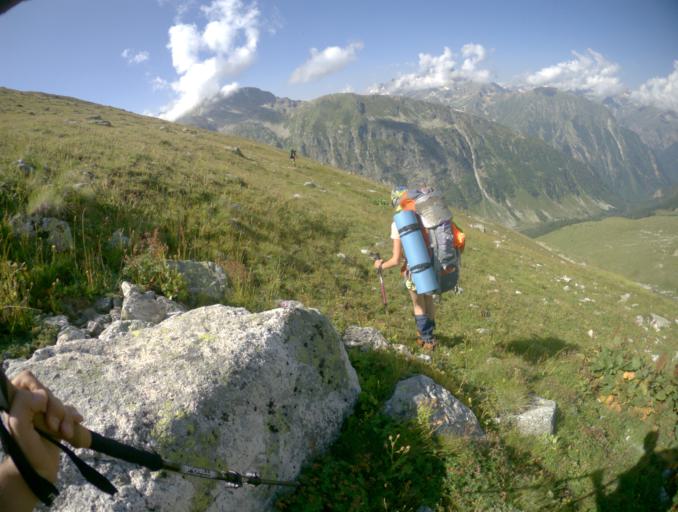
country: RU
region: Karachayevo-Cherkesiya
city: Uchkulan
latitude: 43.3054
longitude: 42.0612
